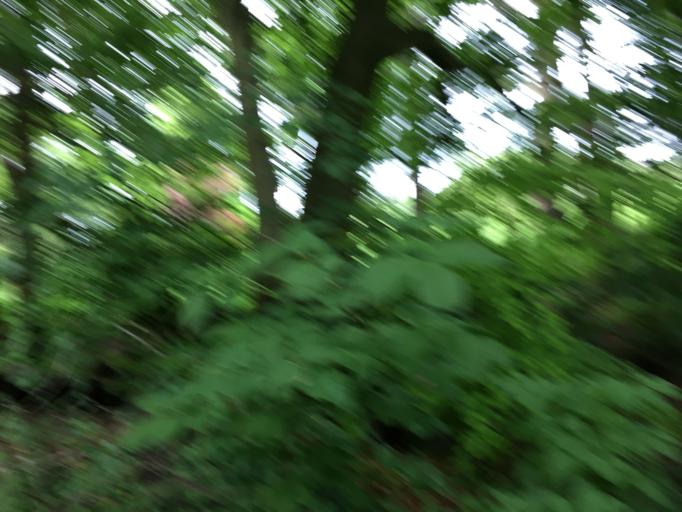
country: GB
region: England
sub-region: Hertfordshire
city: St Albans
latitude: 51.7475
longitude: -0.3580
